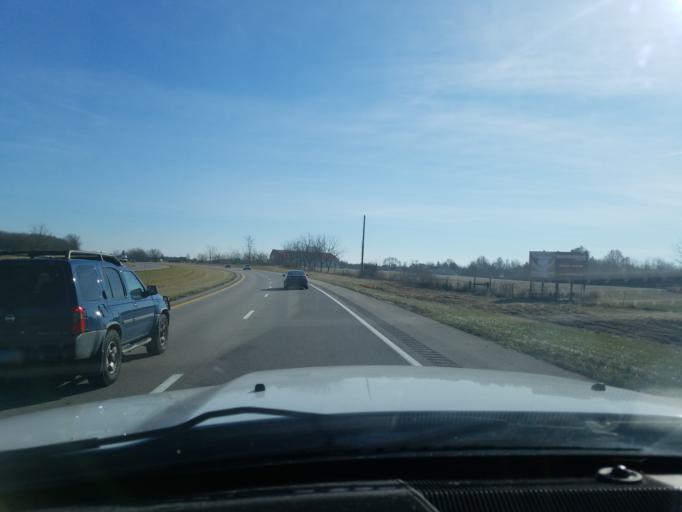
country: US
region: Ohio
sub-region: Adams County
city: Winchester
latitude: 38.9361
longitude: -83.6659
